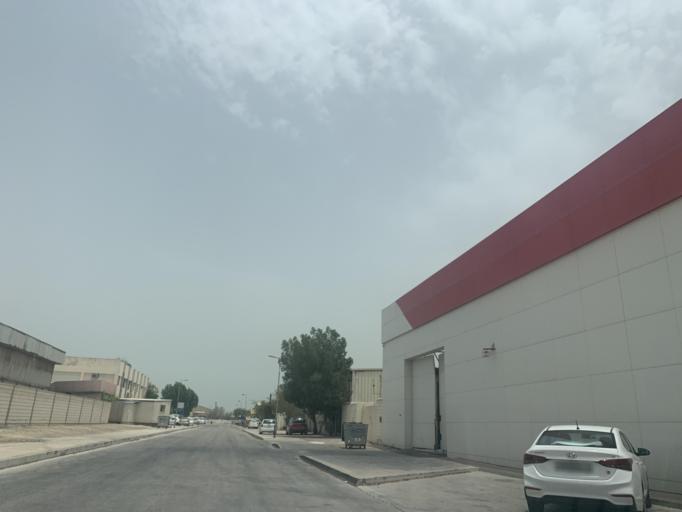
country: BH
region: Northern
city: Sitrah
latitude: 26.1780
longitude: 50.6064
